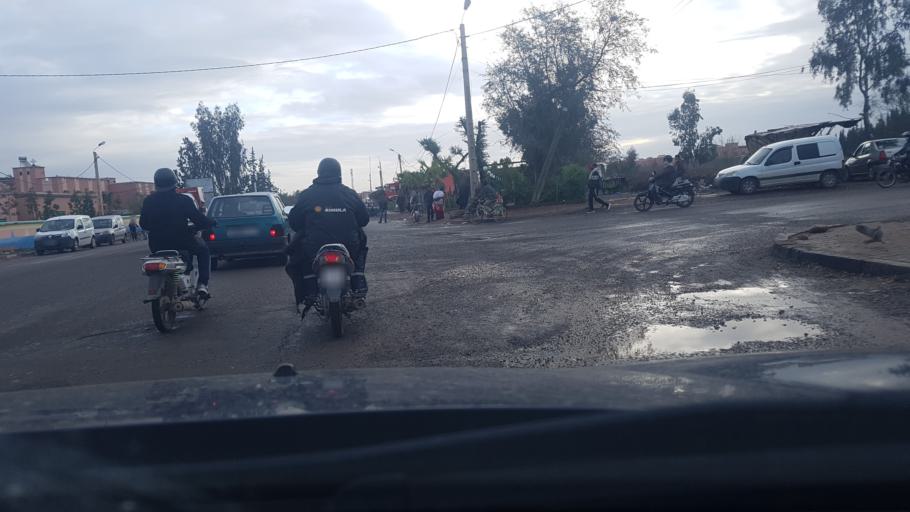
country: MA
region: Marrakech-Tensift-Al Haouz
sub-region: Marrakech
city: Marrakesh
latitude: 31.5726
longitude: -8.0693
